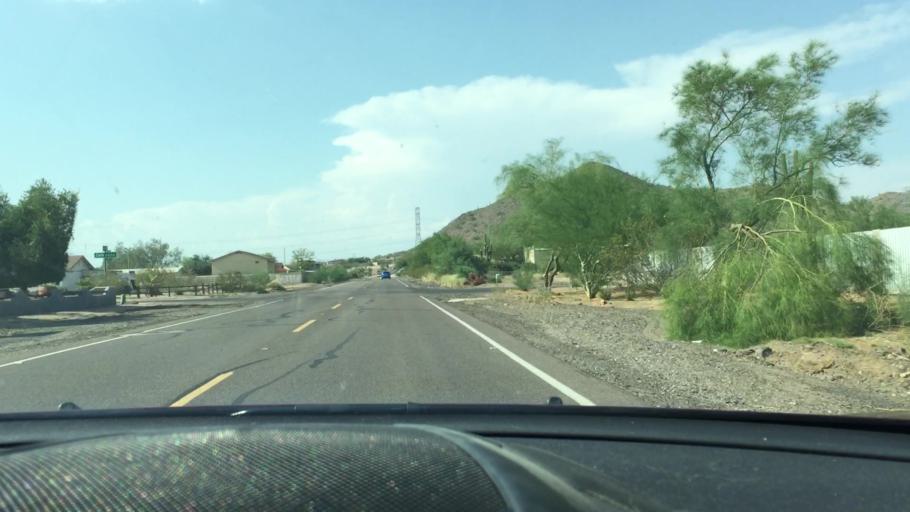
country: US
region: Arizona
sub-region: Maricopa County
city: Sun City West
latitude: 33.7031
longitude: -112.2550
